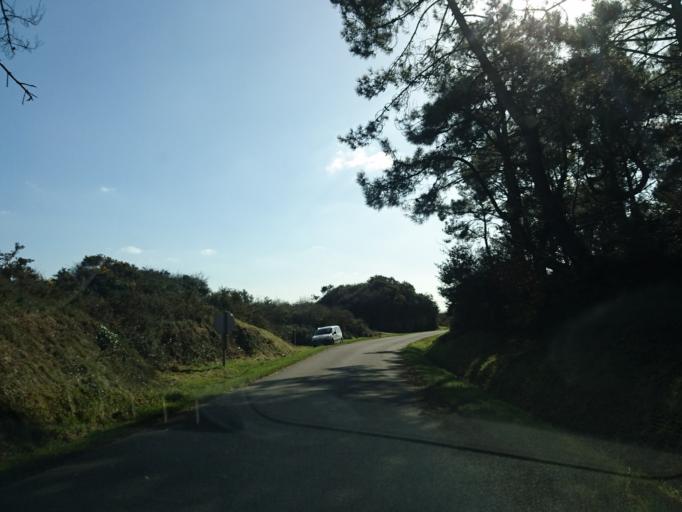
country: FR
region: Brittany
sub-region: Departement du Finistere
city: Roscanvel
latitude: 48.3391
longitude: -4.5354
